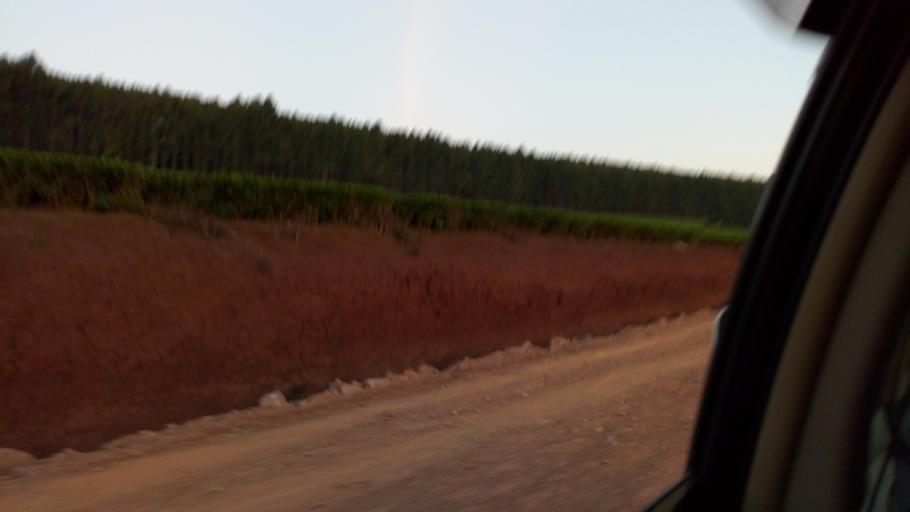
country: KE
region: Kericho
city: Sotik
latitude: -0.6024
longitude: 35.0615
